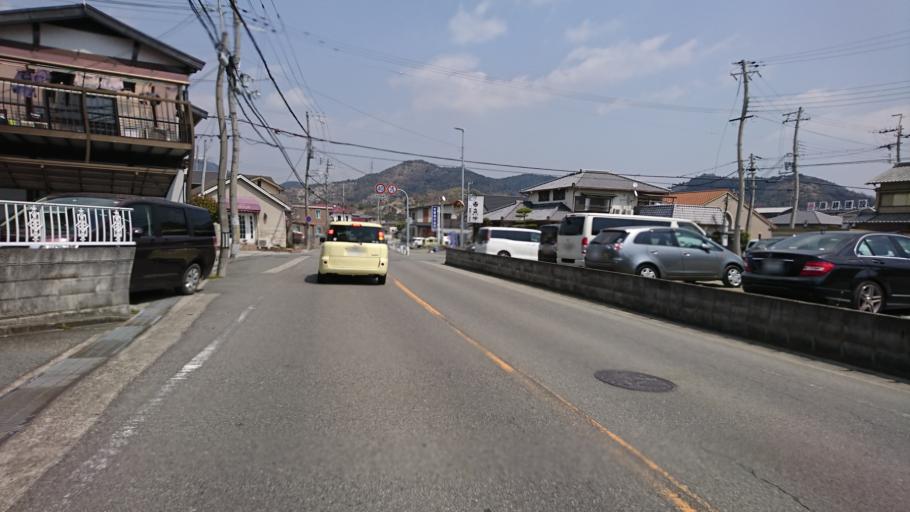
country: JP
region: Hyogo
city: Kakogawacho-honmachi
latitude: 34.7899
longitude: 134.7902
